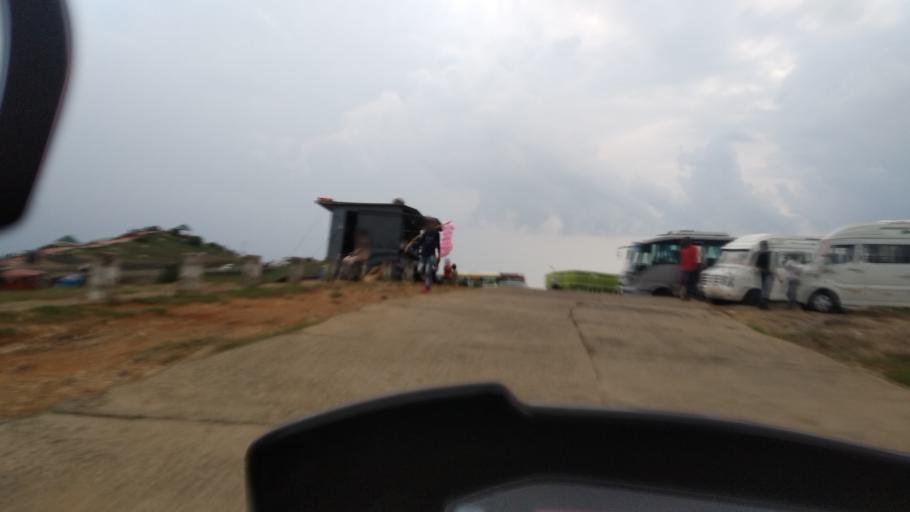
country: IN
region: Tamil Nadu
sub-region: Theni
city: Gudalur
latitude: 9.5500
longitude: 77.0320
